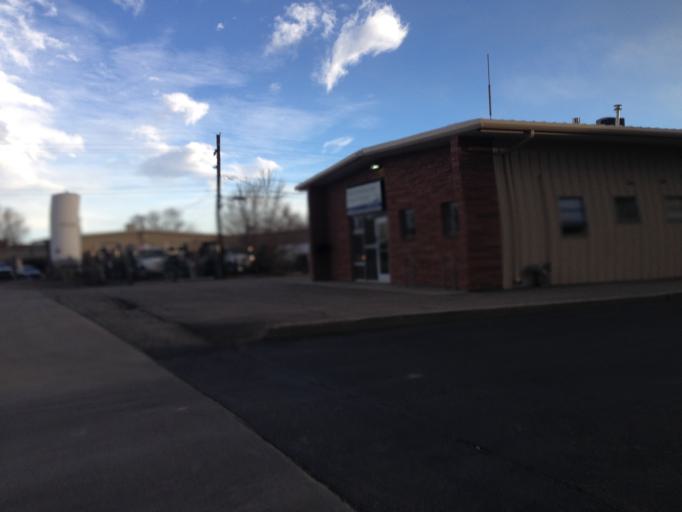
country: US
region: Colorado
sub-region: Boulder County
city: Boulder
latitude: 40.0192
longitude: -105.2463
